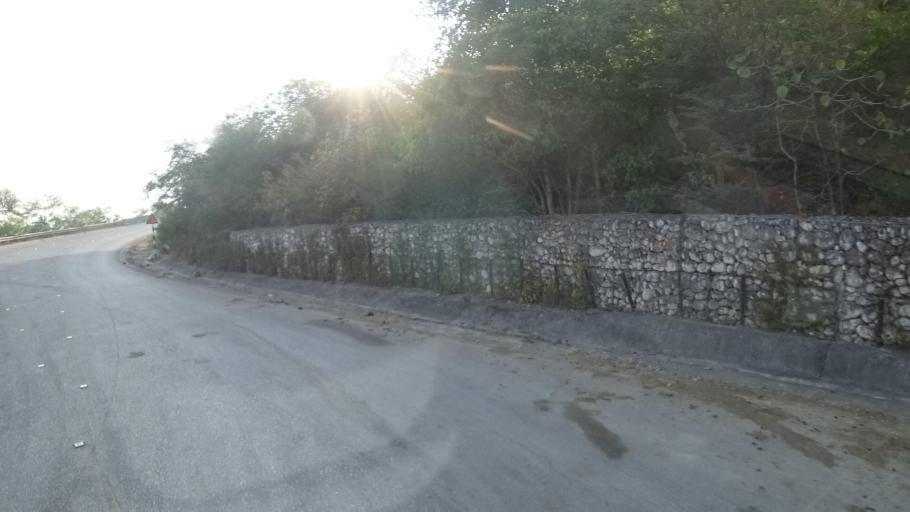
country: YE
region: Al Mahrah
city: Hawf
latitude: 16.7646
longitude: 53.3395
